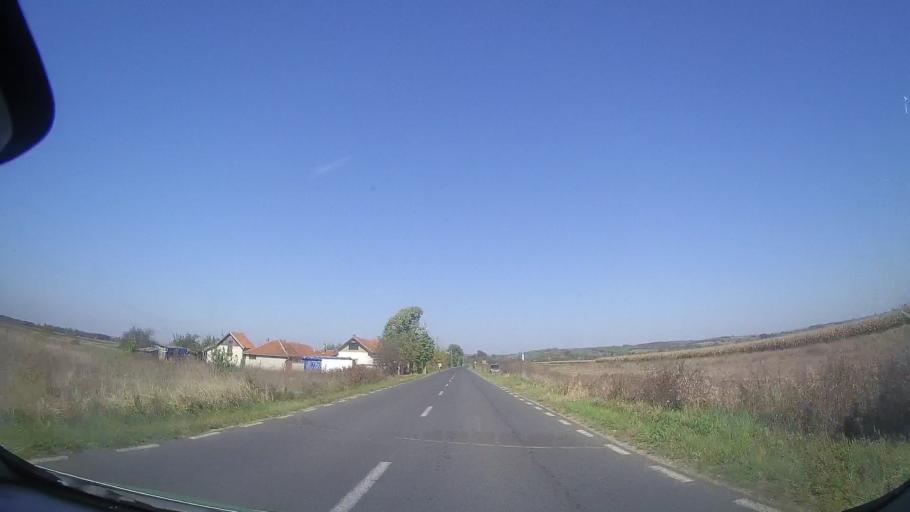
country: RO
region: Timis
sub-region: Comuna Balint
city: Balint
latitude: 45.8030
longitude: 21.8622
